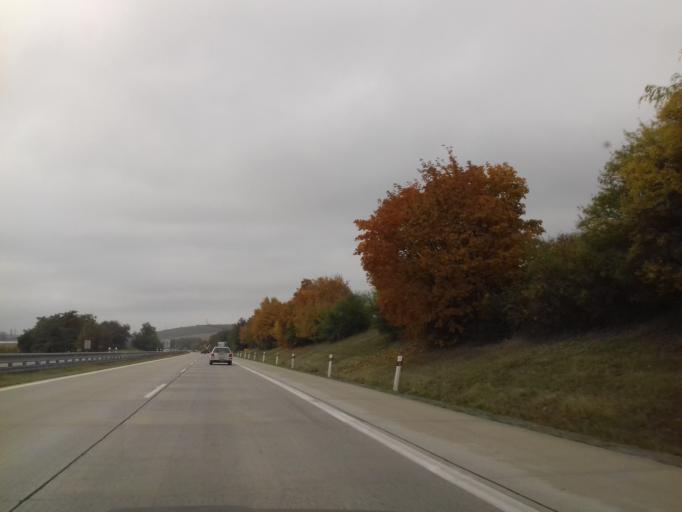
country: CZ
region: South Moravian
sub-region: Okres Breclav
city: Hustopece
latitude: 48.9209
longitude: 16.7671
